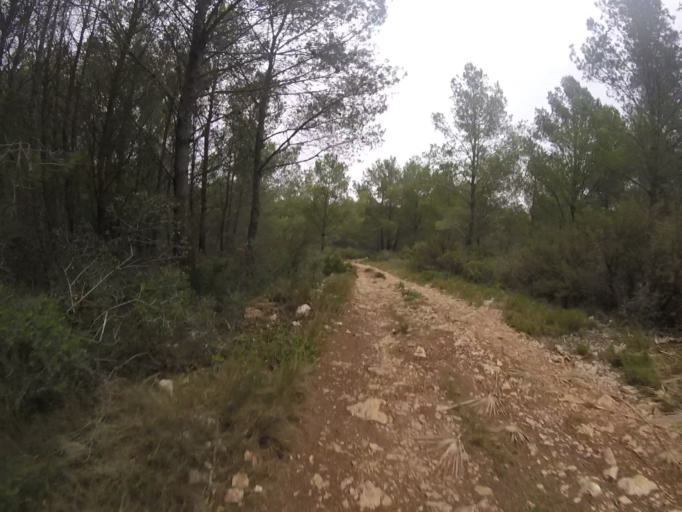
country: ES
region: Valencia
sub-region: Provincia de Castello
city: Alcoceber
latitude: 40.2860
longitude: 0.2853
